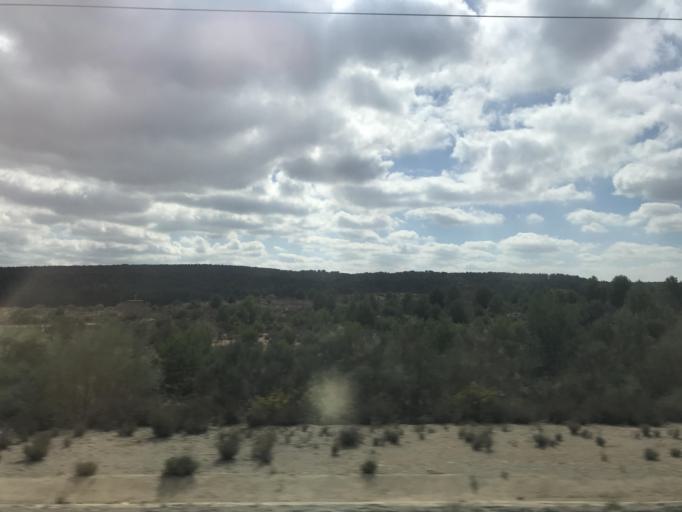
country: ES
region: Castille-La Mancha
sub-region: Provincia de Albacete
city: Almansa
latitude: 38.8743
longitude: -1.1722
